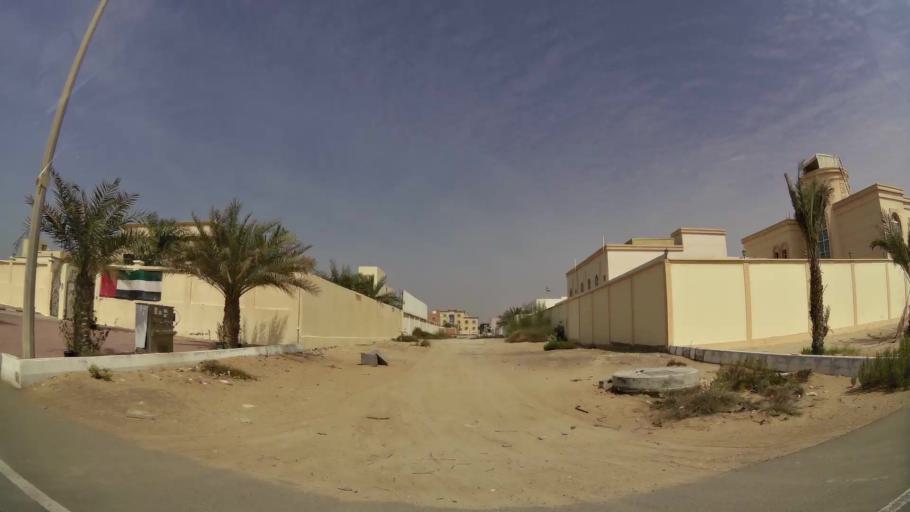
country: AE
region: Abu Dhabi
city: Abu Dhabi
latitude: 24.5444
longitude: 54.6617
